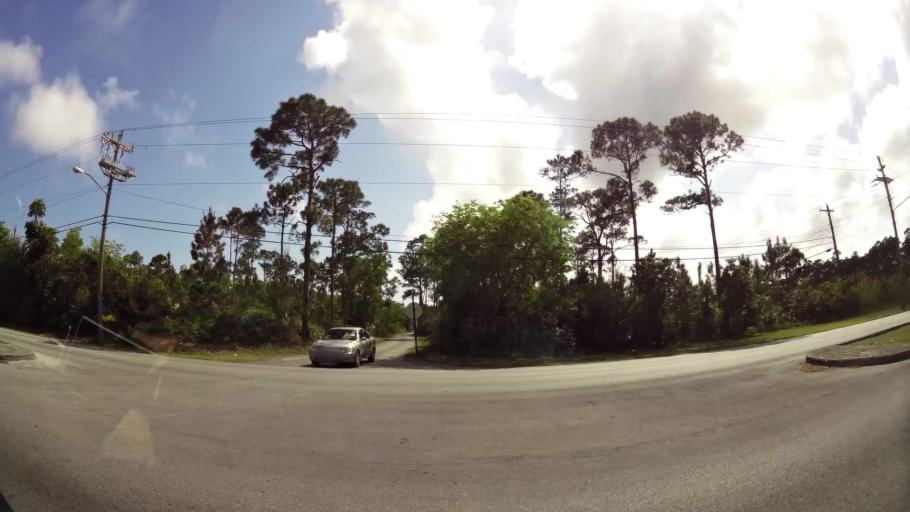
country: BS
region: Freeport
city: Freeport
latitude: 26.5210
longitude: -78.6963
